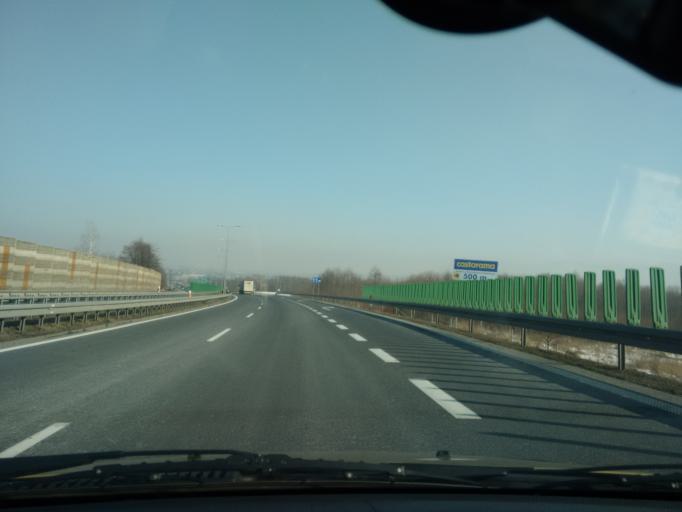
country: PL
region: Silesian Voivodeship
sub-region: Bielsko-Biala
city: Bielsko-Biala
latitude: 49.8473
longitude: 19.0242
